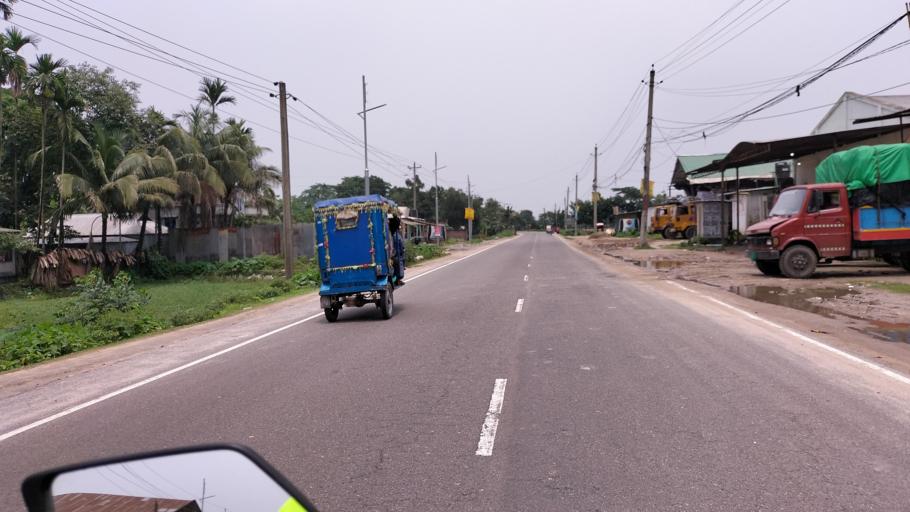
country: BD
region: Dhaka
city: Mymensingh
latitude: 24.7734
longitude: 90.4599
